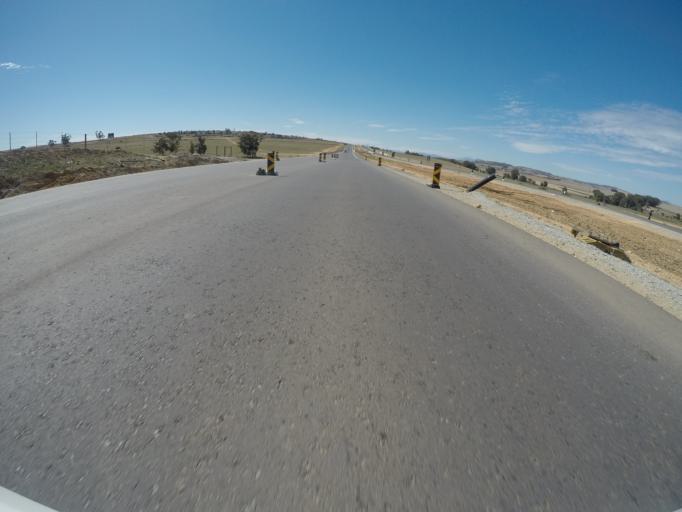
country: ZA
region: Western Cape
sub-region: West Coast District Municipality
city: Malmesbury
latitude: -33.4779
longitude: 18.6854
